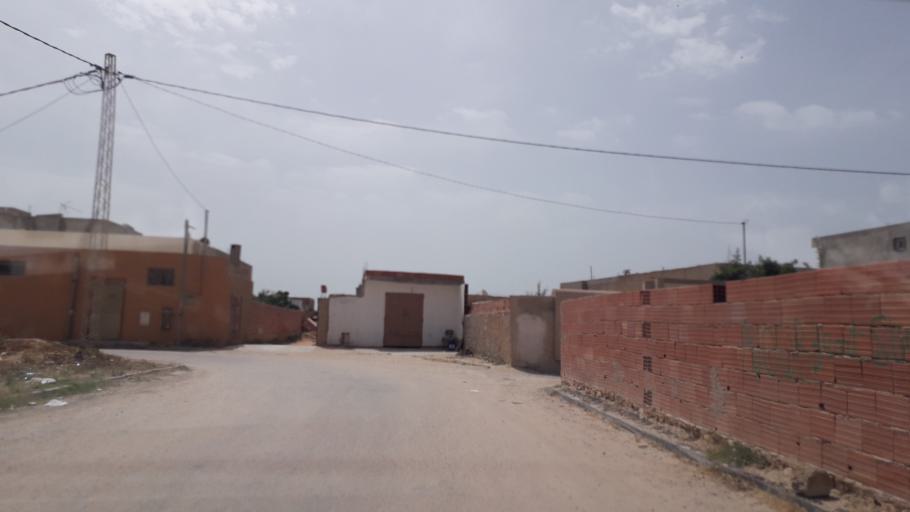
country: TN
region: Safaqis
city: Al Qarmadah
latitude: 34.8409
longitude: 10.7759
